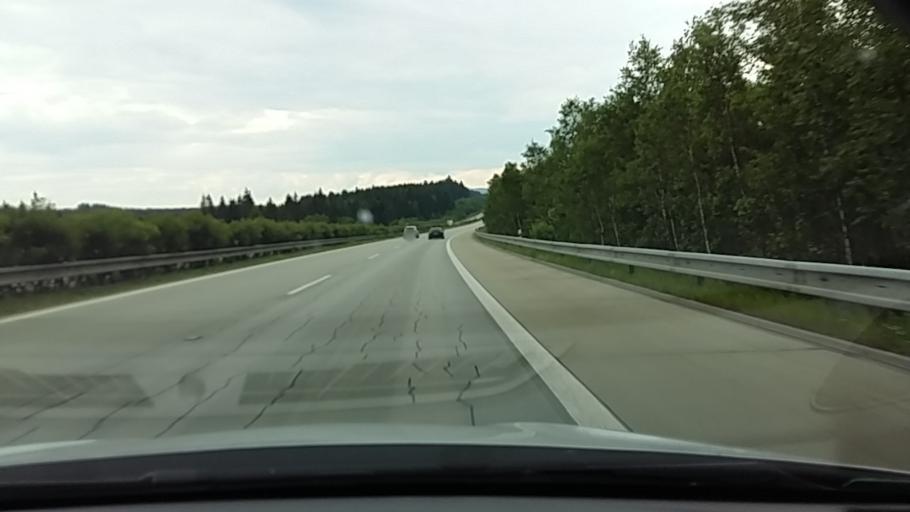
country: CZ
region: Plzensky
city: Primda
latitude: 49.6807
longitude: 12.6412
